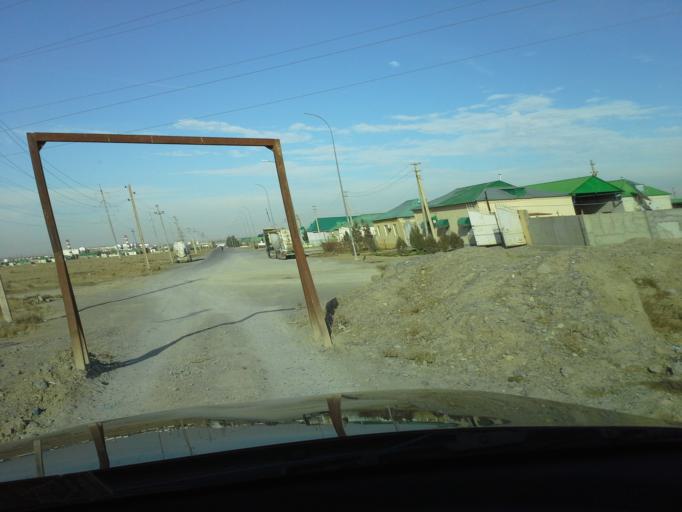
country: TM
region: Ahal
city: Abadan
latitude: 38.0425
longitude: 58.1628
